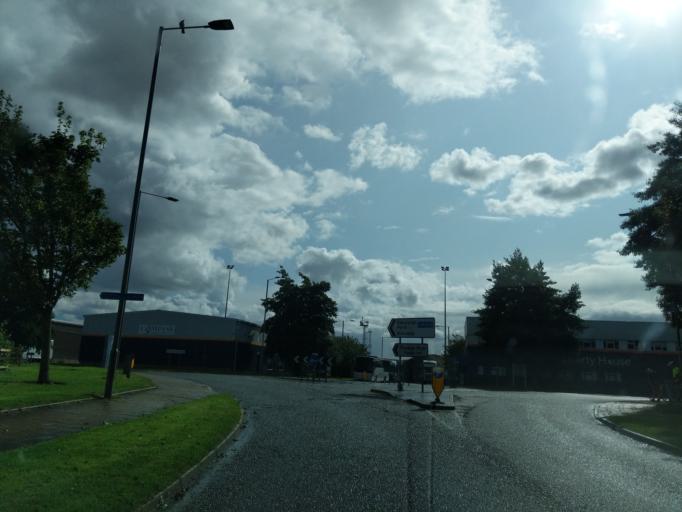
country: GB
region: Scotland
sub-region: Fife
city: Rosyth
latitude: 56.0264
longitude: -3.4383
